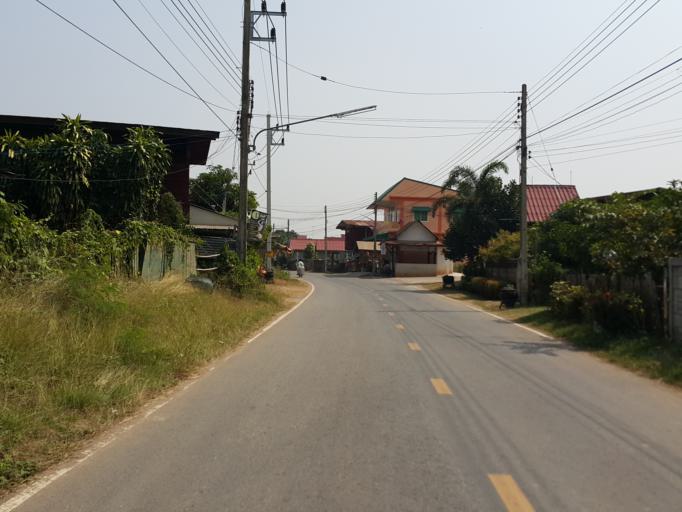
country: TH
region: Sukhothai
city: Thung Saliam
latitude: 17.3265
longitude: 99.5100
